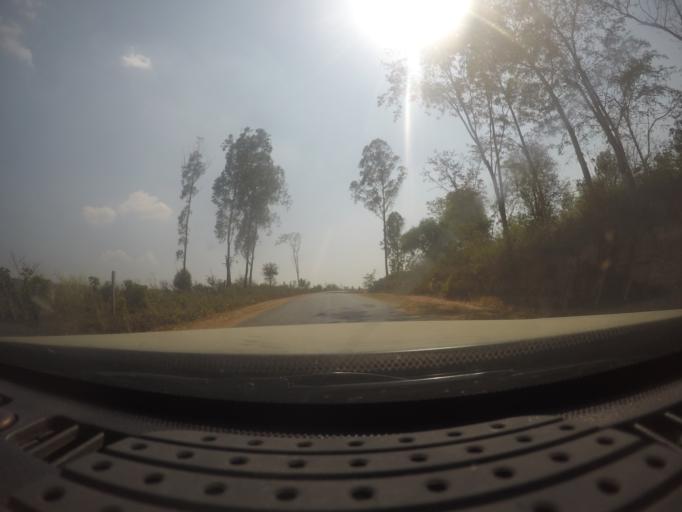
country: MM
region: Shan
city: Taunggyi
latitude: 21.0787
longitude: 96.5044
